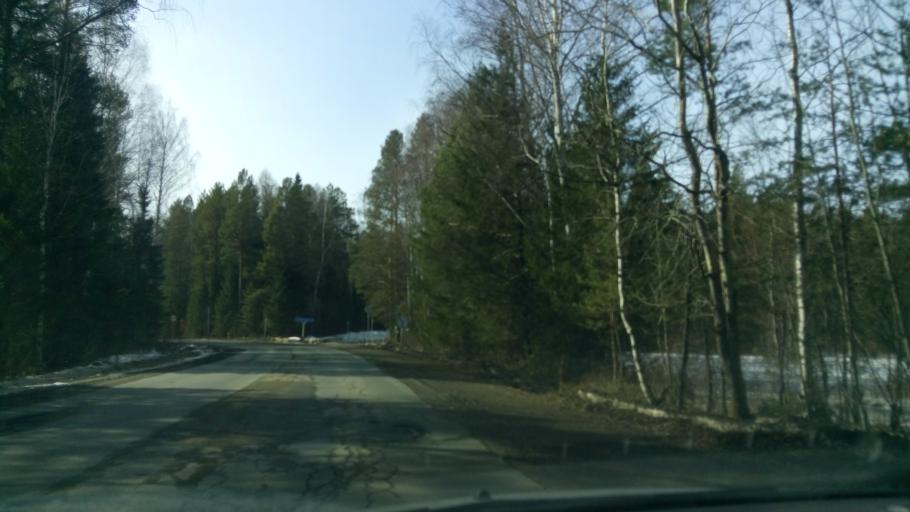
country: RU
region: Sverdlovsk
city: Chernoistochinsk
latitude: 57.7326
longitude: 59.7885
